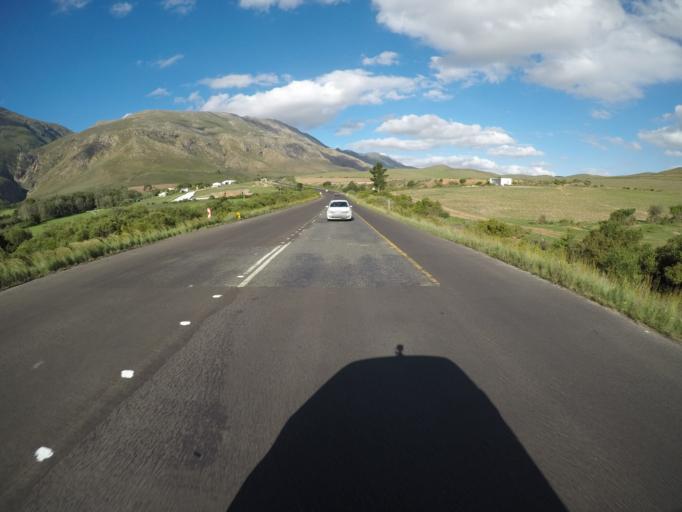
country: ZA
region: Western Cape
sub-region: Cape Winelands District Municipality
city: Ashton
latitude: -33.8731
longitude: 20.1531
